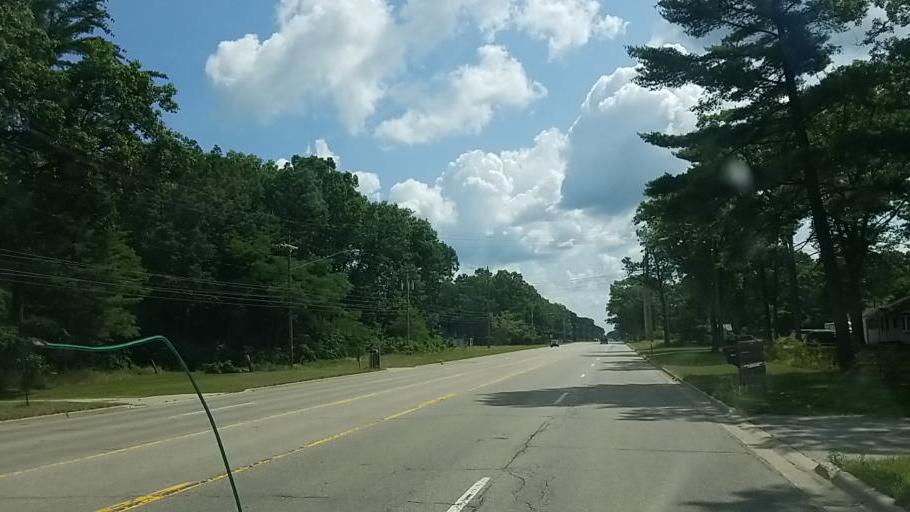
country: US
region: Michigan
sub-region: Muskegon County
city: Wolf Lake
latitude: 43.2349
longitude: -86.0845
